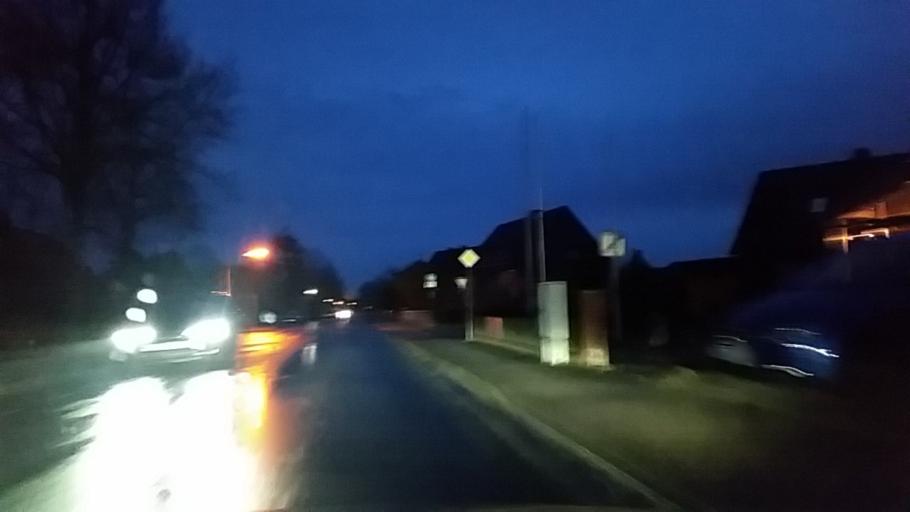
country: DE
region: Lower Saxony
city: Meine
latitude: 52.3511
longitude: 10.5562
